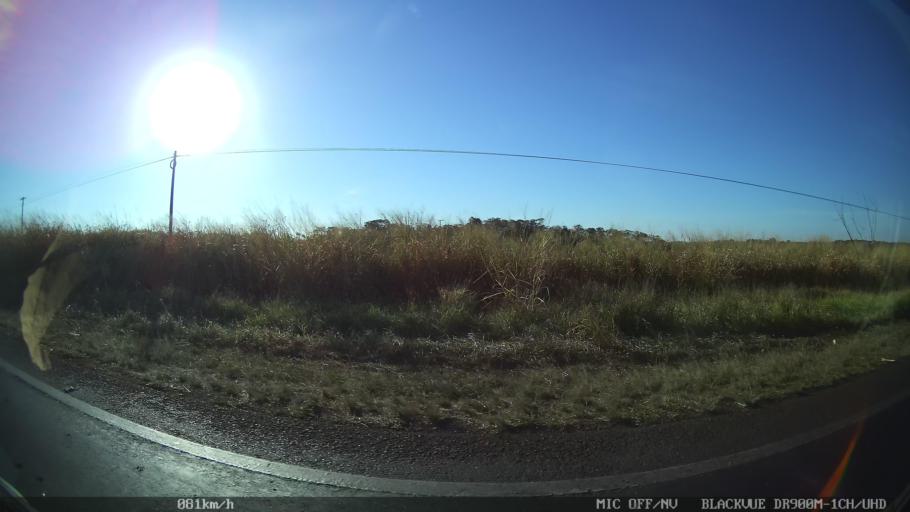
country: BR
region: Sao Paulo
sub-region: Guapiacu
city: Guapiacu
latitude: -20.7467
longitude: -49.1206
